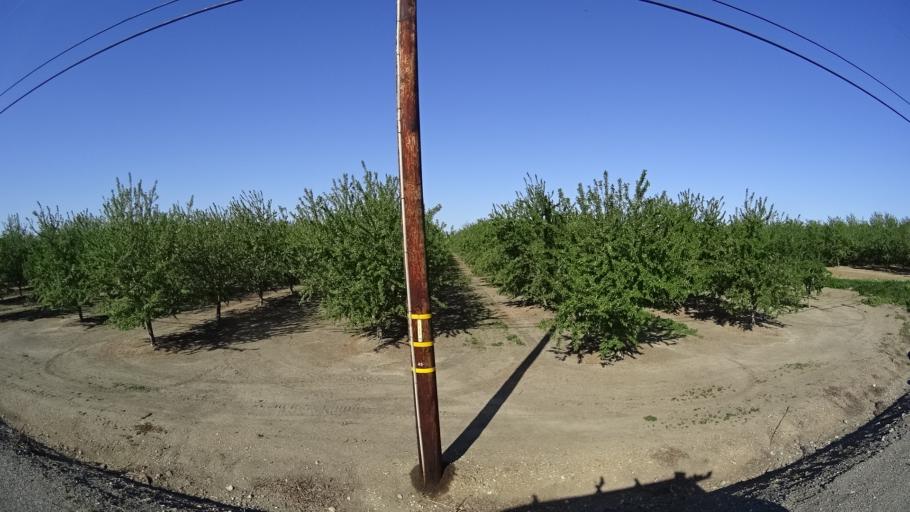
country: US
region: California
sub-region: Glenn County
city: Orland
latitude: 39.8014
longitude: -122.1041
